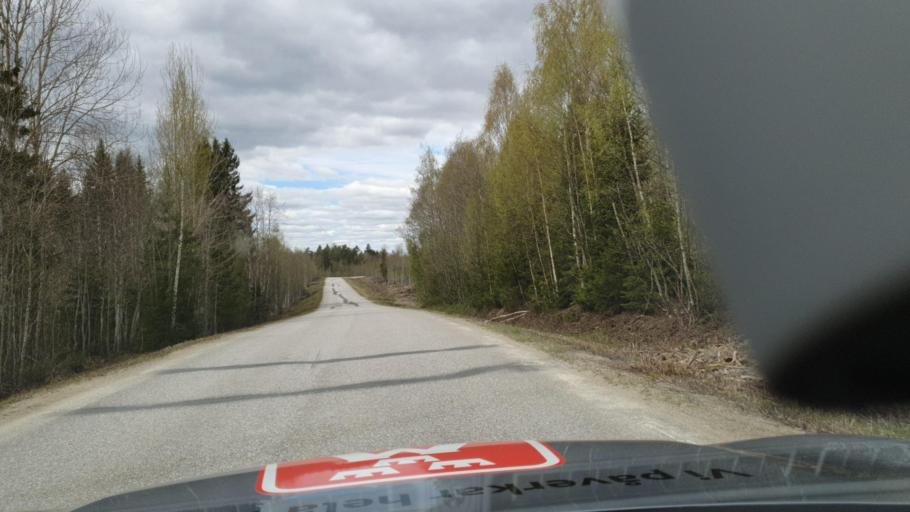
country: SE
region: Vaesternorrland
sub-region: OErnskoeldsviks Kommun
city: Ornskoldsvik
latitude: 63.6422
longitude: 18.7704
